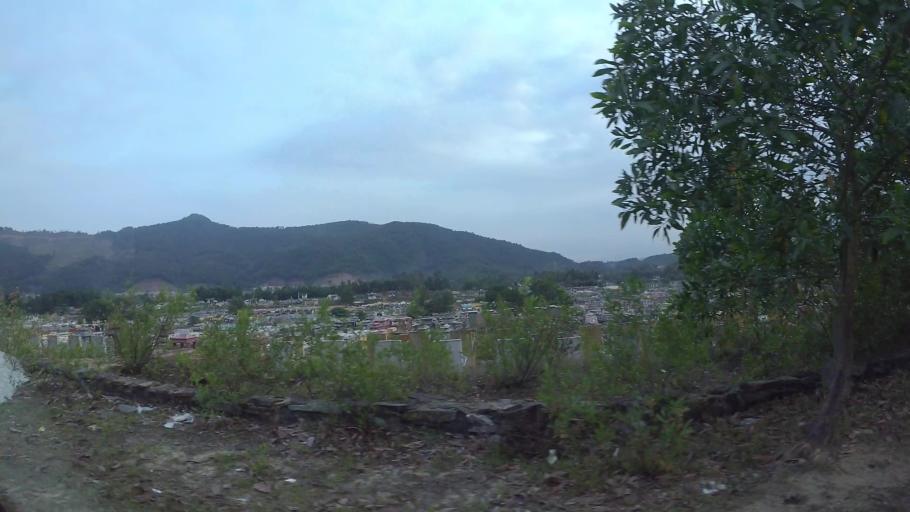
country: VN
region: Da Nang
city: Lien Chieu
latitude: 16.0621
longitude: 108.1180
